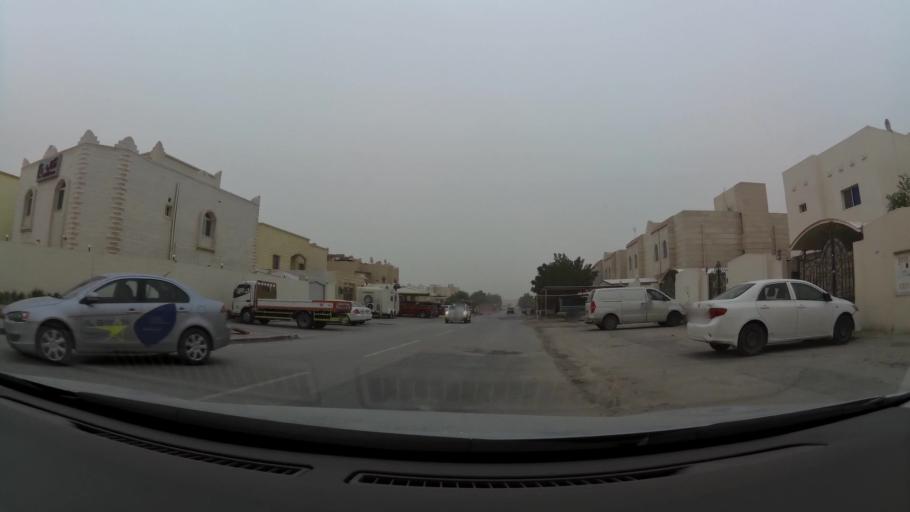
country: QA
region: Baladiyat ad Dawhah
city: Doha
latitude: 25.2315
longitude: 51.4987
